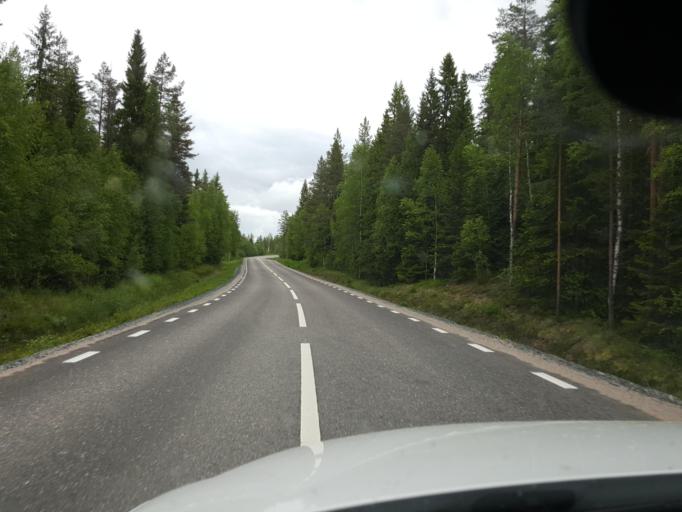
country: SE
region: Gaevleborg
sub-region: Ljusdals Kommun
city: Farila
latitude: 61.7492
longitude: 15.3678
